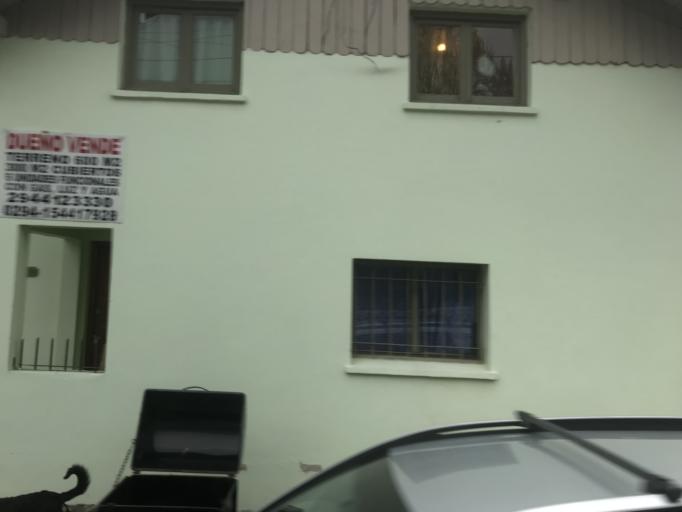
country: AR
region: Rio Negro
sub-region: Departamento de Bariloche
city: San Carlos de Bariloche
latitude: -41.1379
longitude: -71.3147
